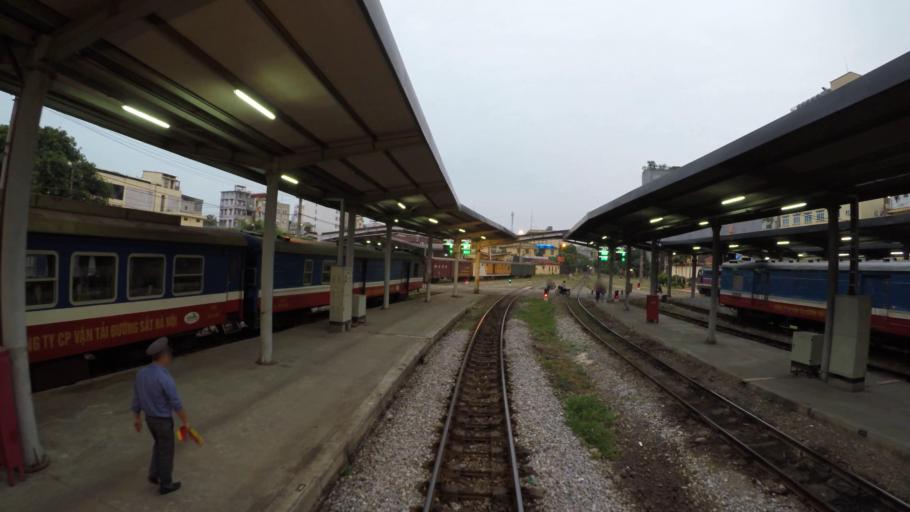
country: VN
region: Ha Noi
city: Hanoi
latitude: 21.0270
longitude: 105.8411
